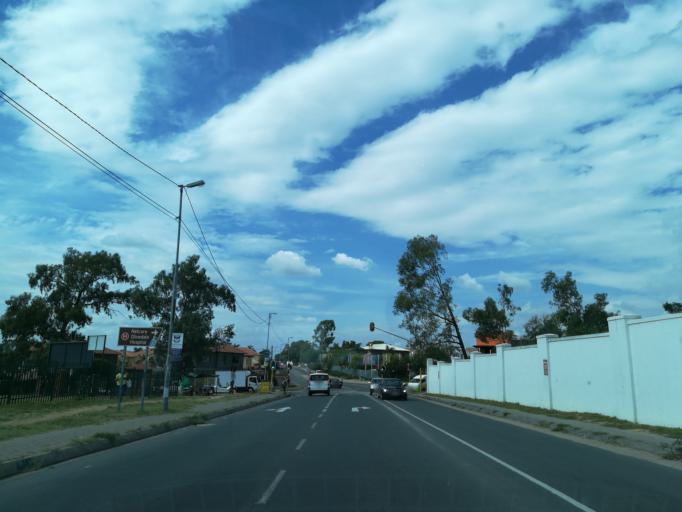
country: ZA
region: Gauteng
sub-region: West Rand District Municipality
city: Muldersdriseloop
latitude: -26.0558
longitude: 27.9631
